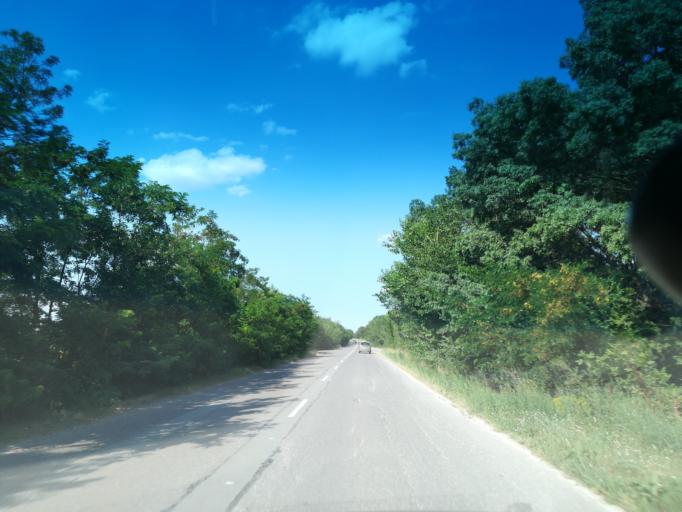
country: BG
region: Stara Zagora
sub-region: Obshtina Chirpan
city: Chirpan
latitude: 42.2446
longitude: 25.4085
